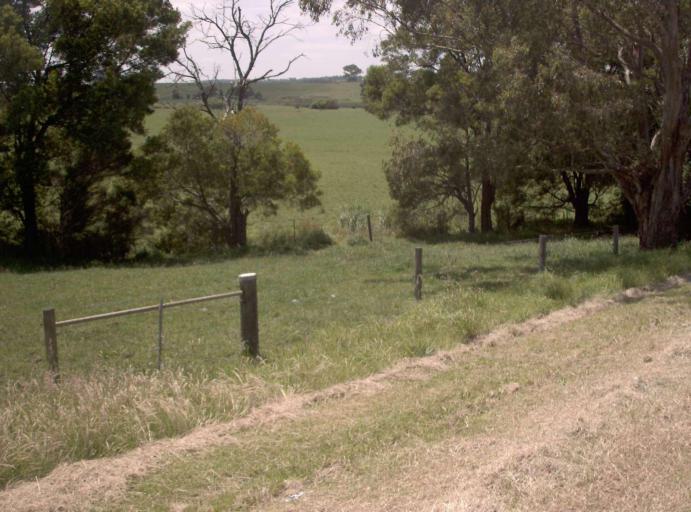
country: AU
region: Victoria
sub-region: Baw Baw
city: Warragul
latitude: -38.4791
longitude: 145.9721
